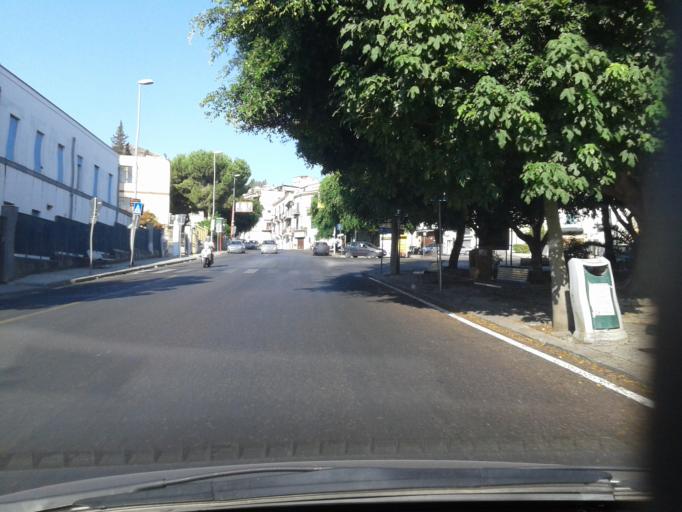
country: IT
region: Sicily
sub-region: Palermo
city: Palermo
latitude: 38.1093
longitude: 13.3097
